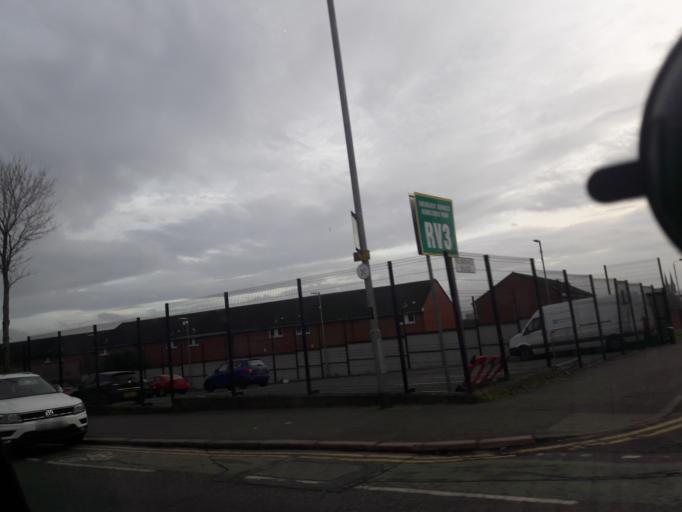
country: GB
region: Northern Ireland
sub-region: City of Belfast
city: Belfast
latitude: 54.6086
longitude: -5.9416
